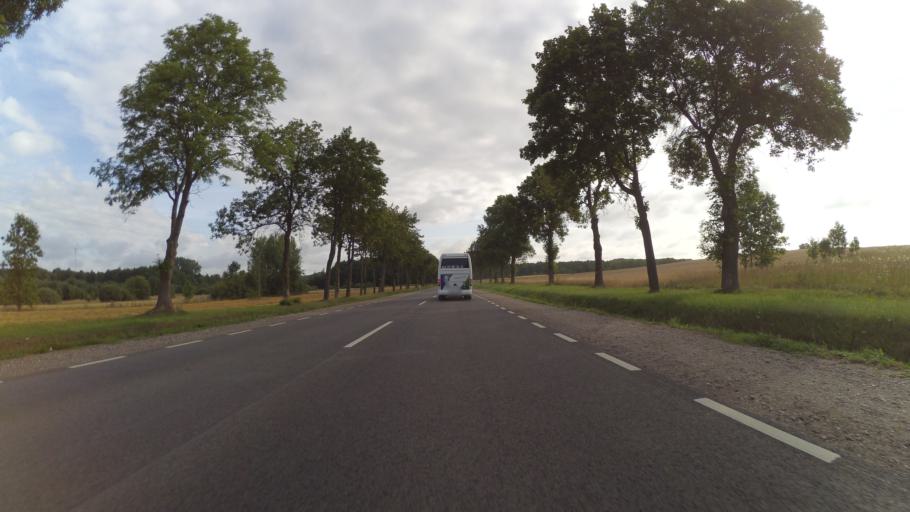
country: PL
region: Podlasie
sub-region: Powiat sokolski
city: Kuznica
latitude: 53.4591
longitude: 23.5771
